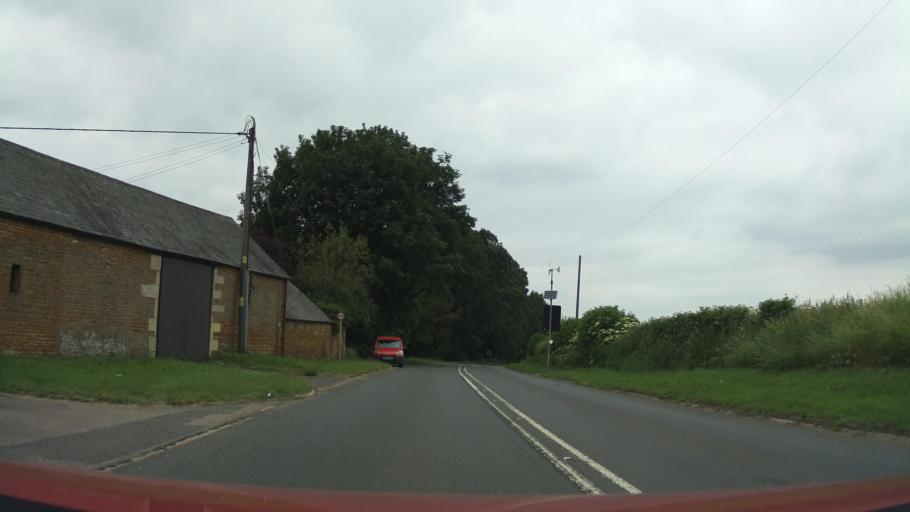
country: GB
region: England
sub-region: District of Rutland
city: Preston
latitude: 52.6150
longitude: -0.7136
